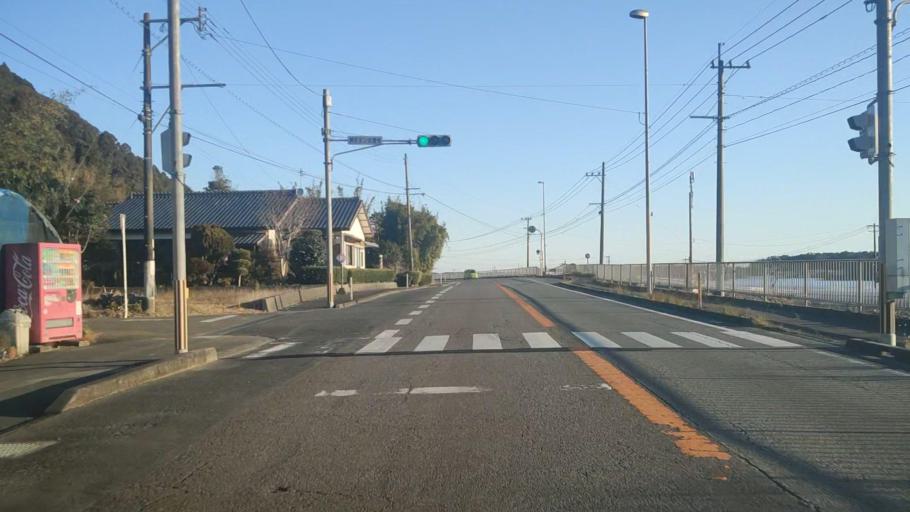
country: JP
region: Miyazaki
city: Takanabe
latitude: 32.0851
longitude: 131.5113
